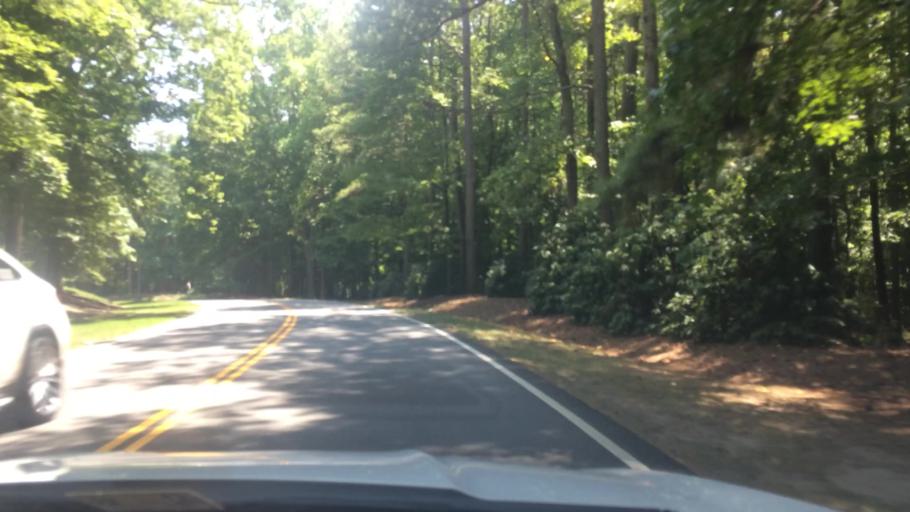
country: US
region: Virginia
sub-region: City of Williamsburg
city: Williamsburg
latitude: 37.2403
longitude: -76.6612
